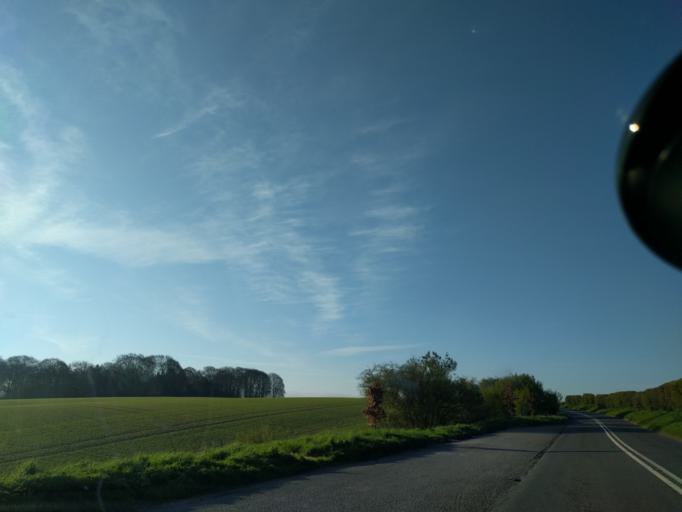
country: GB
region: England
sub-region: Wiltshire
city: Woodford
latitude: 51.1391
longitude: -1.8582
